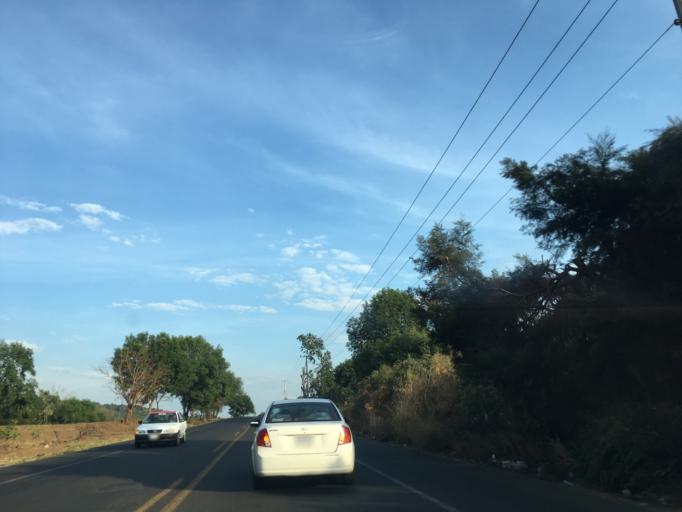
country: MX
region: Michoacan
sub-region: Tingueindin
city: Tingueindin
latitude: 19.7216
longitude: -102.4823
